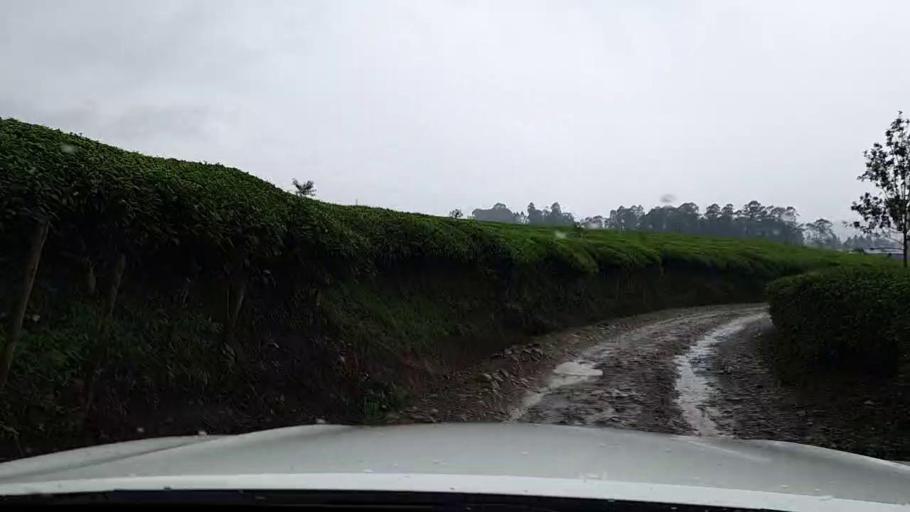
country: RW
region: Western Province
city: Cyangugu
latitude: -2.4550
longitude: 29.0393
